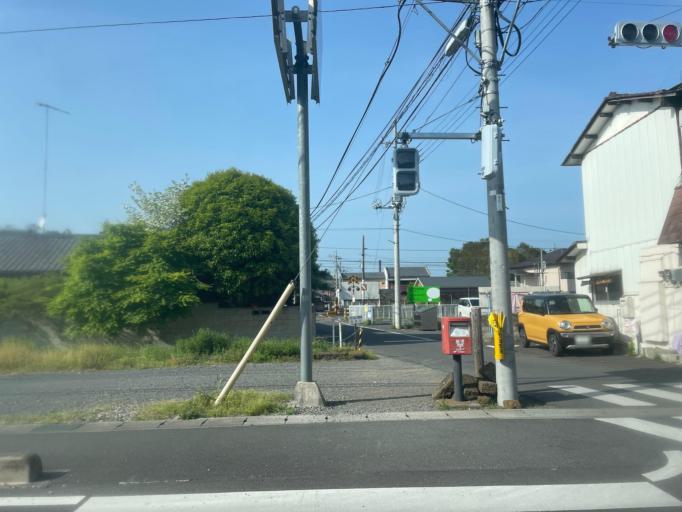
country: JP
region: Tochigi
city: Sano
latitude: 36.3159
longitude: 139.5273
